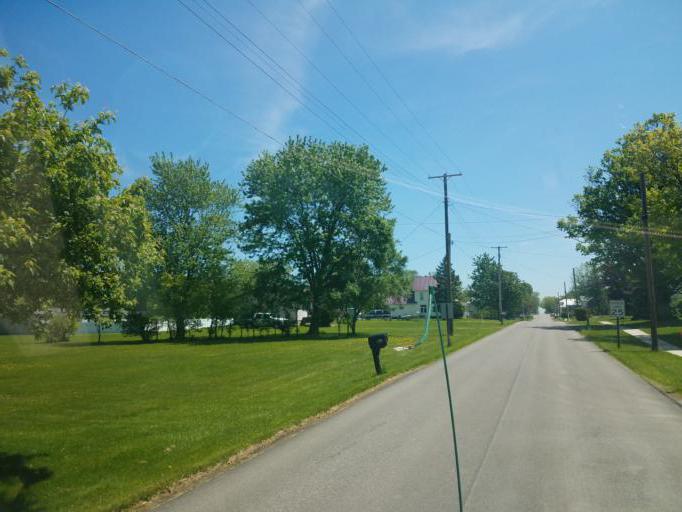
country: US
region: Ohio
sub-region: Wayne County
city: West Salem
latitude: 40.9448
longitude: -82.2185
